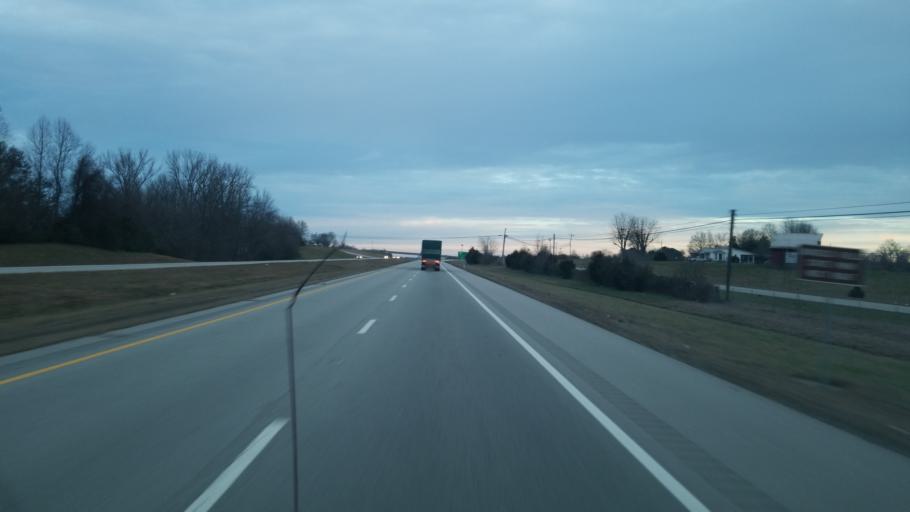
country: US
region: Tennessee
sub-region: Putnam County
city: Cookeville
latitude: 36.0475
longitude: -85.5078
